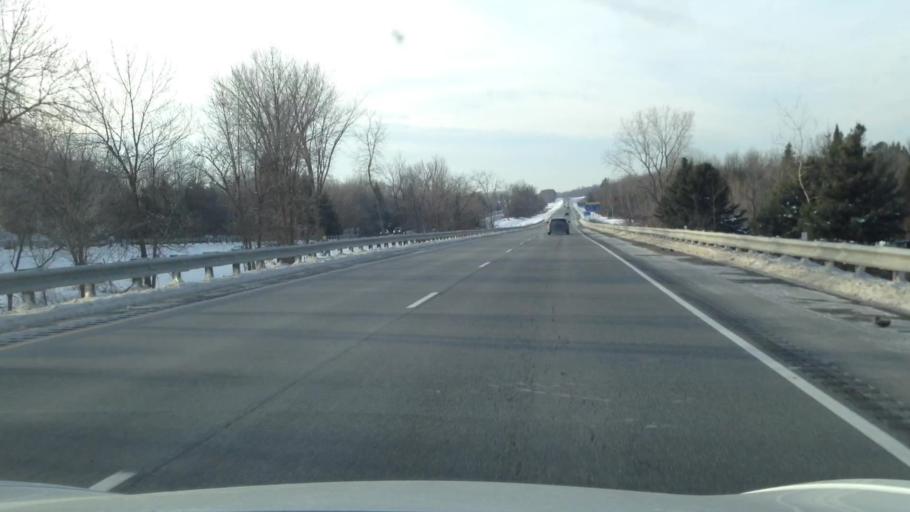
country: CA
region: Quebec
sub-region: Monteregie
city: Rigaud
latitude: 45.5417
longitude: -74.3998
